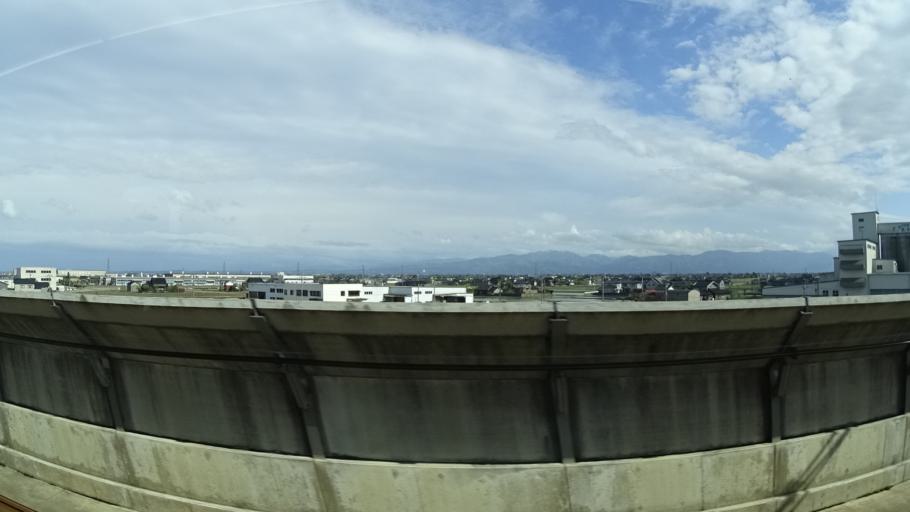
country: JP
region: Toyama
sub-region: Oyabe Shi
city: Oyabe
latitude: 36.6942
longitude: 136.9285
